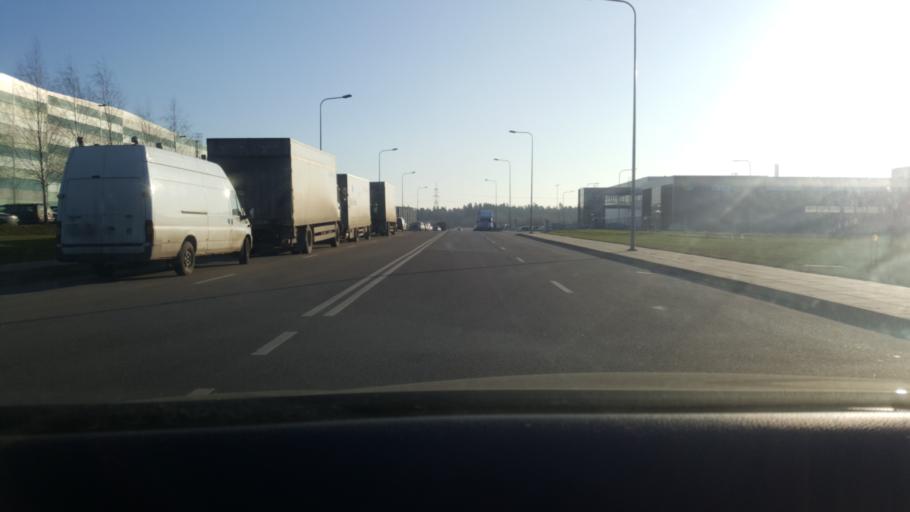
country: LT
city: Ramuciai
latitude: 54.9405
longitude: 24.0101
